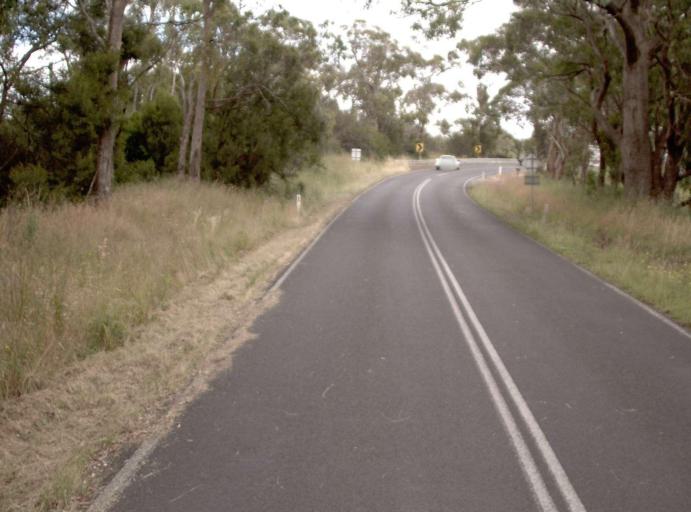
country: AU
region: Victoria
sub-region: Latrobe
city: Moe
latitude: -38.1133
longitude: 146.2508
